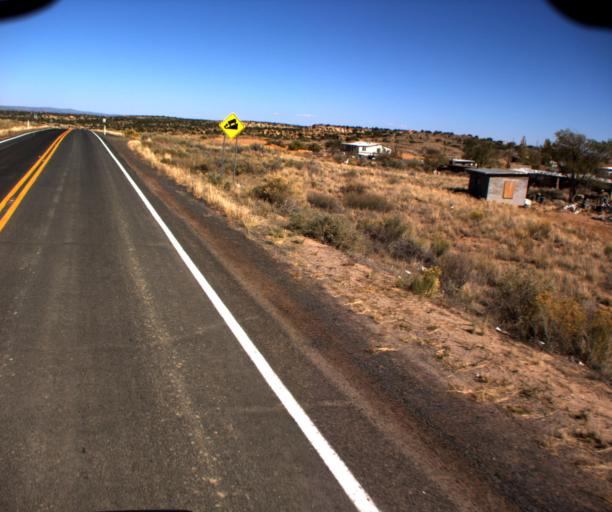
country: US
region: Arizona
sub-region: Navajo County
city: First Mesa
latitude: 35.9247
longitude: -110.6621
